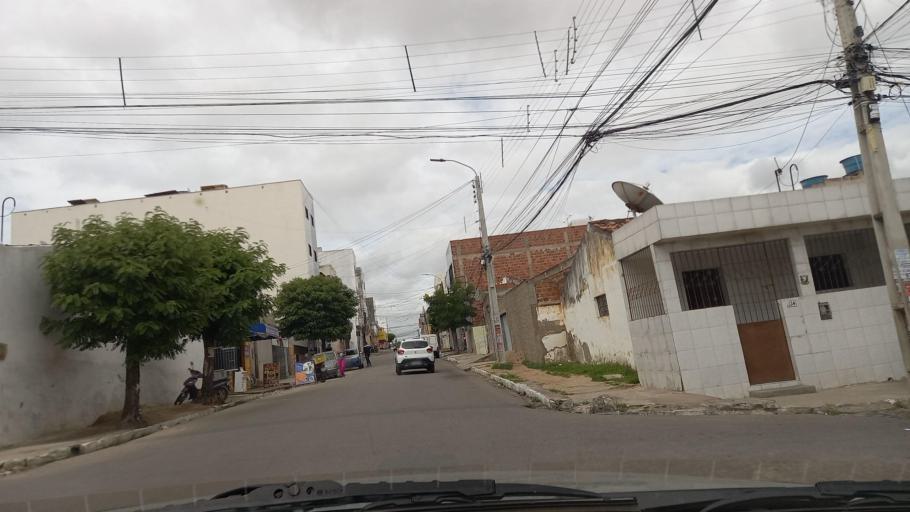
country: BR
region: Pernambuco
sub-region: Caruaru
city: Caruaru
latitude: -8.2753
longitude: -35.9601
